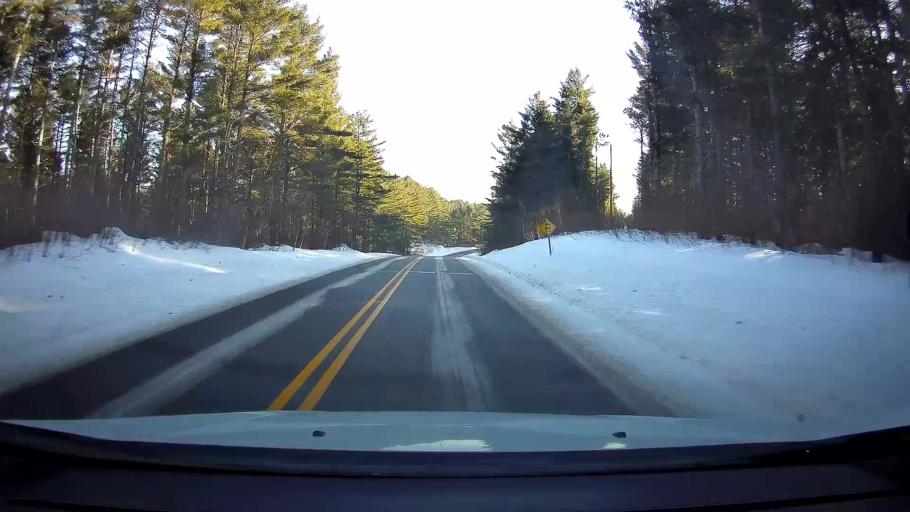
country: US
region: Wisconsin
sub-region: Sawyer County
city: Little Round Lake
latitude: 46.1115
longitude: -91.3103
